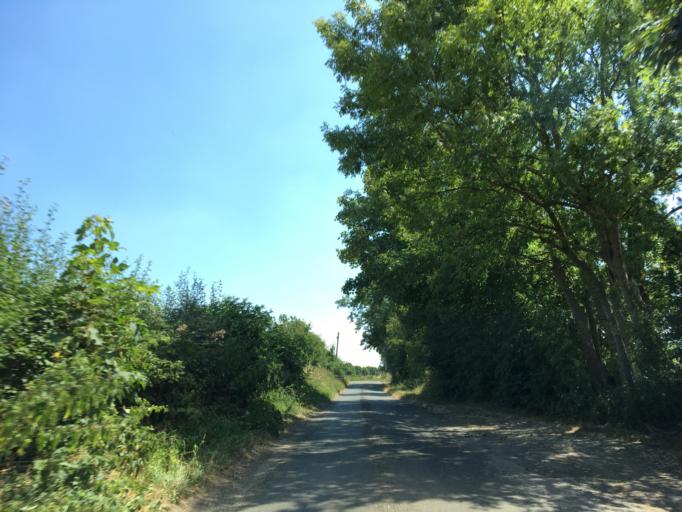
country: GB
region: England
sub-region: Gloucestershire
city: Chalford
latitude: 51.6977
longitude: -2.1031
